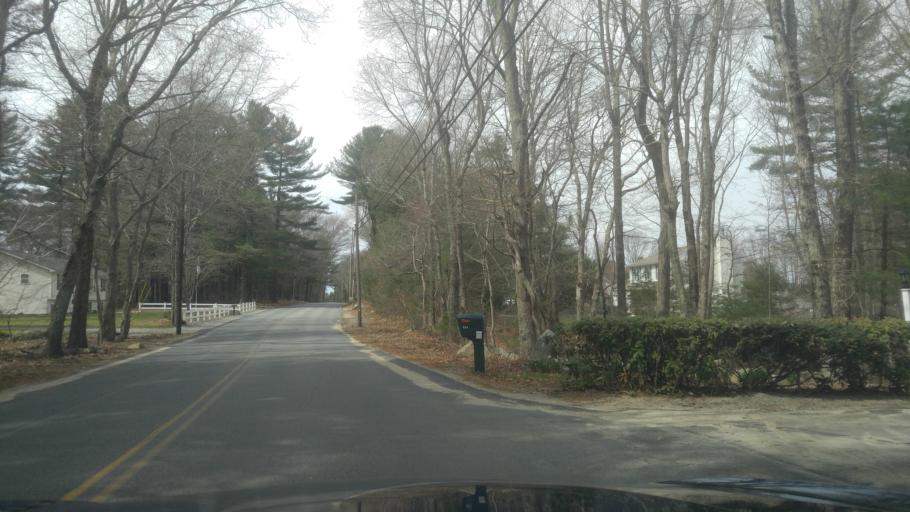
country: US
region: Rhode Island
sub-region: Washington County
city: Exeter
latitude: 41.6242
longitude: -71.5659
